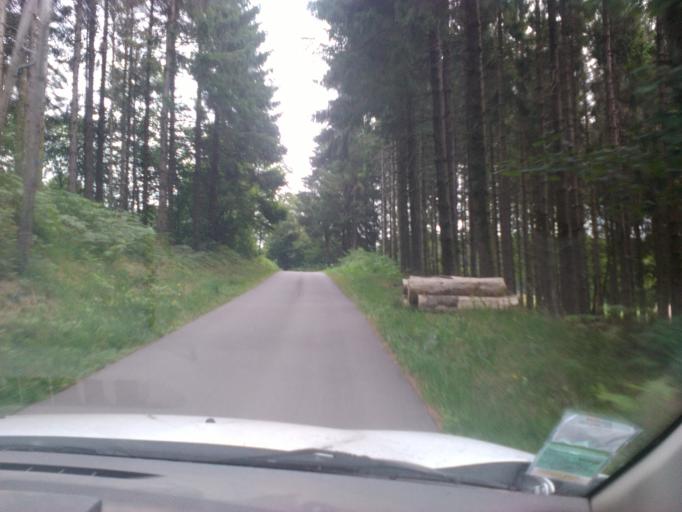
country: FR
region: Lorraine
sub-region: Departement des Vosges
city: Le Tholy
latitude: 48.0978
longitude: 6.7244
